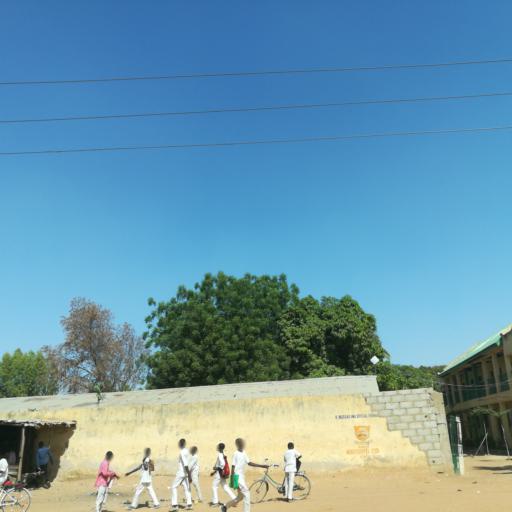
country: NG
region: Kano
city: Kano
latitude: 11.9971
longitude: 8.5300
